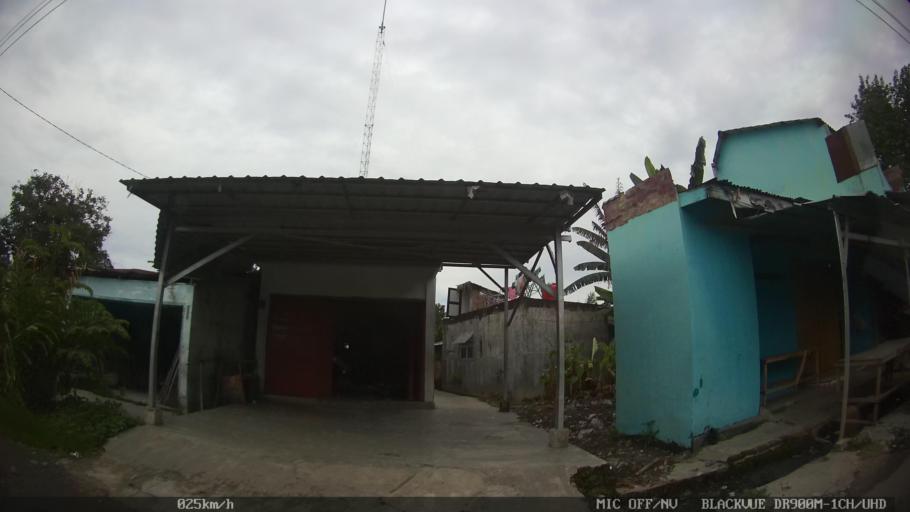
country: ID
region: North Sumatra
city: Sunggal
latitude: 3.6559
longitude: 98.5929
